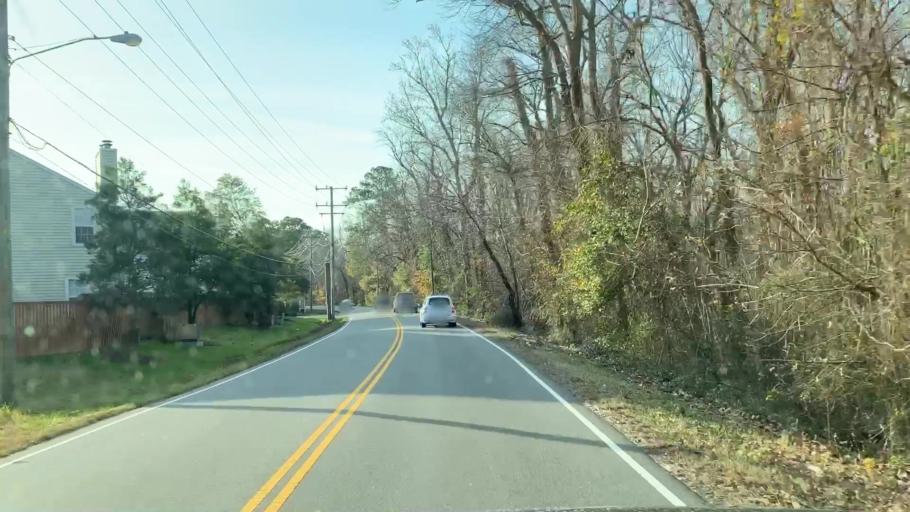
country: US
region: Virginia
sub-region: City of Chesapeake
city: Chesapeake
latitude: 36.7823
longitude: -76.1587
